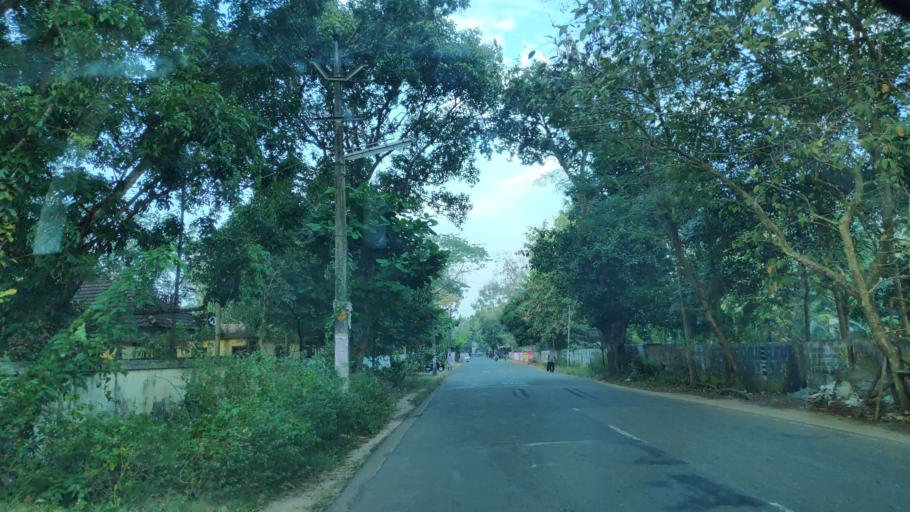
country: IN
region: Kerala
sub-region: Alappuzha
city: Shertallai
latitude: 9.6276
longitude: 76.3687
